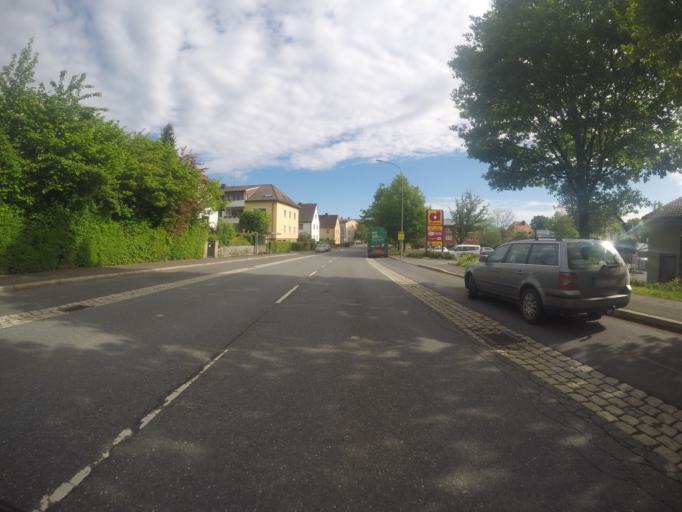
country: DE
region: Bavaria
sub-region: Upper Franconia
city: Schonwald
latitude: 50.1975
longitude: 12.0911
